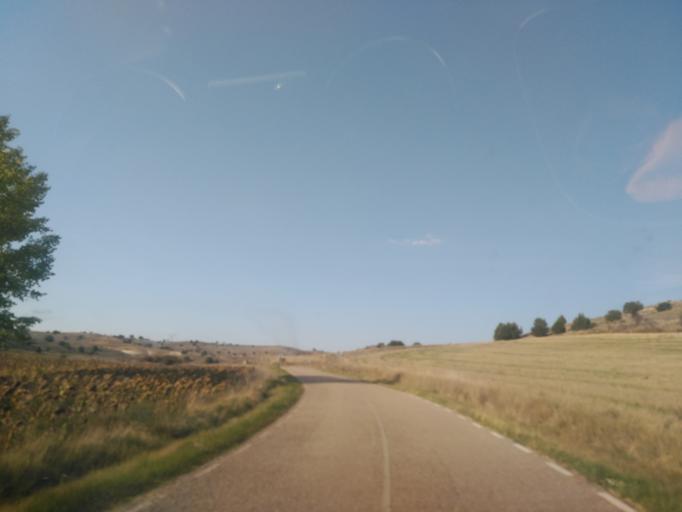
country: ES
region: Castille and Leon
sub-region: Provincia de Burgos
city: Penaranda de Duero
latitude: 41.6381
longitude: -3.4860
